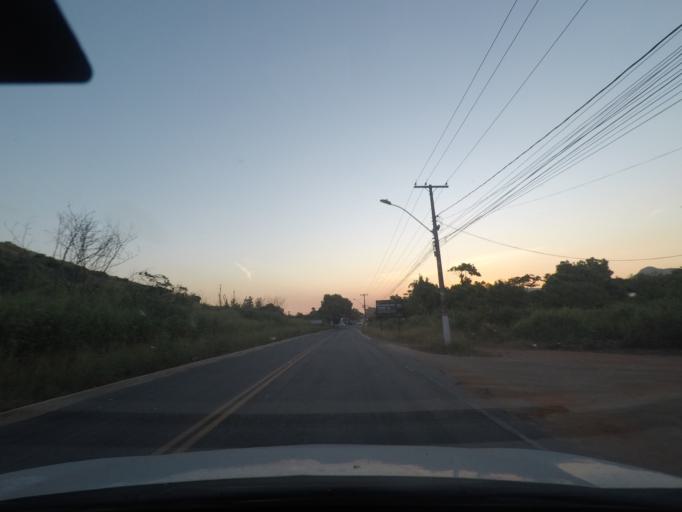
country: BR
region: Rio de Janeiro
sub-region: Niteroi
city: Niteroi
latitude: -22.9555
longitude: -42.9772
